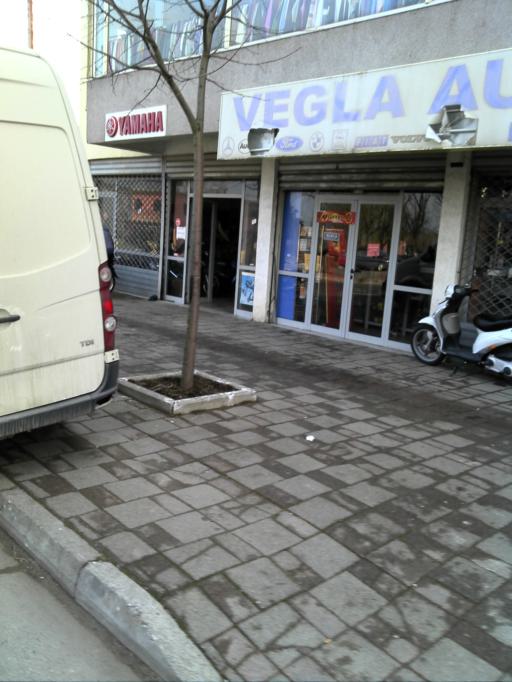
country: AL
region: Shkoder
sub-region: Rrethi i Shkodres
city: Shkoder
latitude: 42.0509
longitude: 19.4945
